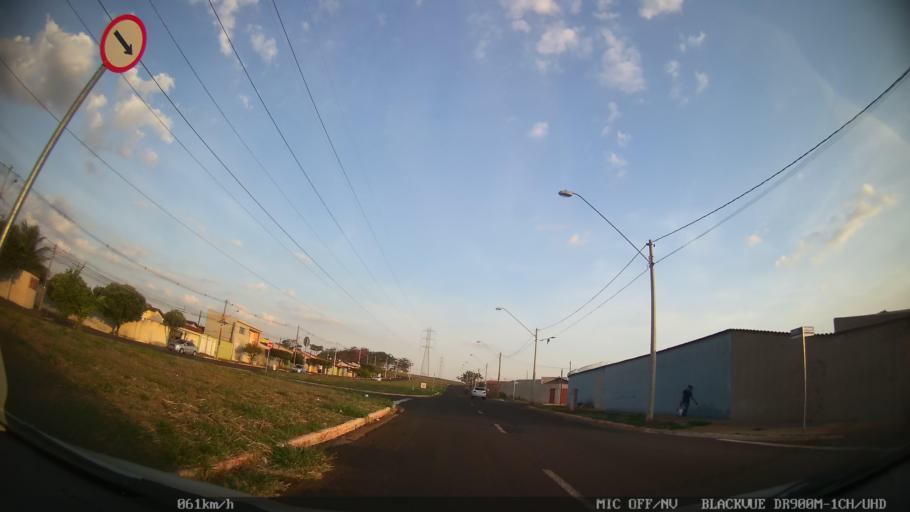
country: BR
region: Sao Paulo
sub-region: Ribeirao Preto
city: Ribeirao Preto
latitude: -21.1388
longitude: -47.8577
